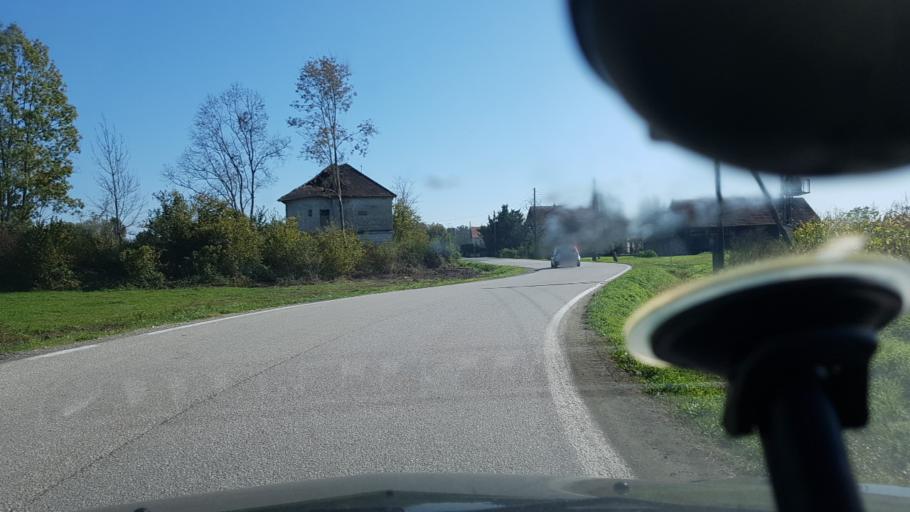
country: HR
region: Zagrebacka
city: Lupoglav
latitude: 45.7111
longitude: 16.3326
